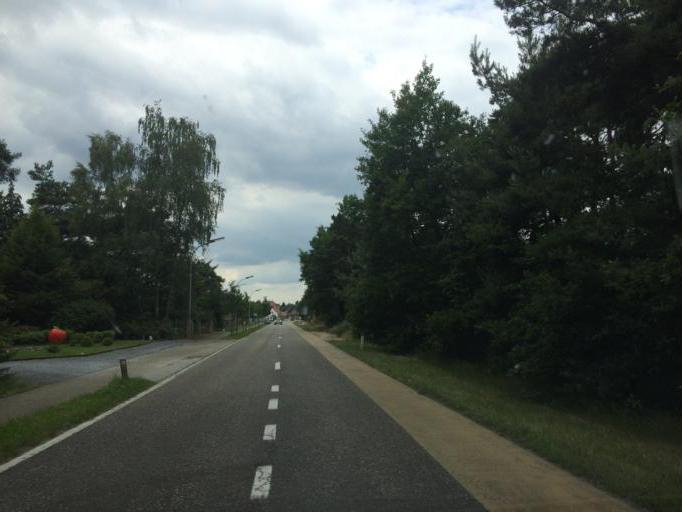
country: BE
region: Flanders
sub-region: Provincie Antwerpen
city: Mol
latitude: 51.2032
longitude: 5.1468
